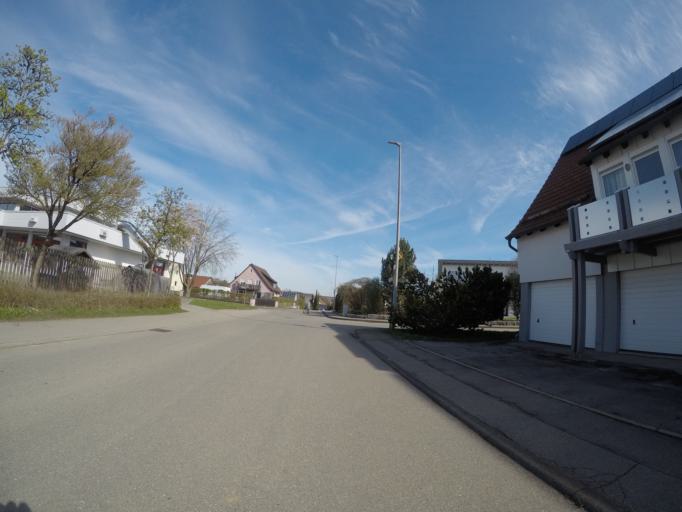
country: DE
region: Baden-Wuerttemberg
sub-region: Tuebingen Region
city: Laichingen
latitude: 48.4865
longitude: 9.6931
